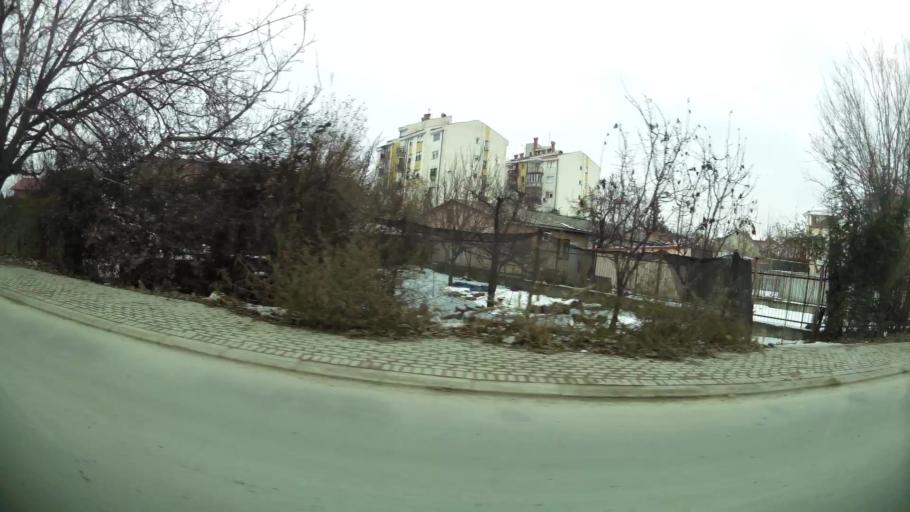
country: MK
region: Butel
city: Butel
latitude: 42.0363
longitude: 21.4441
